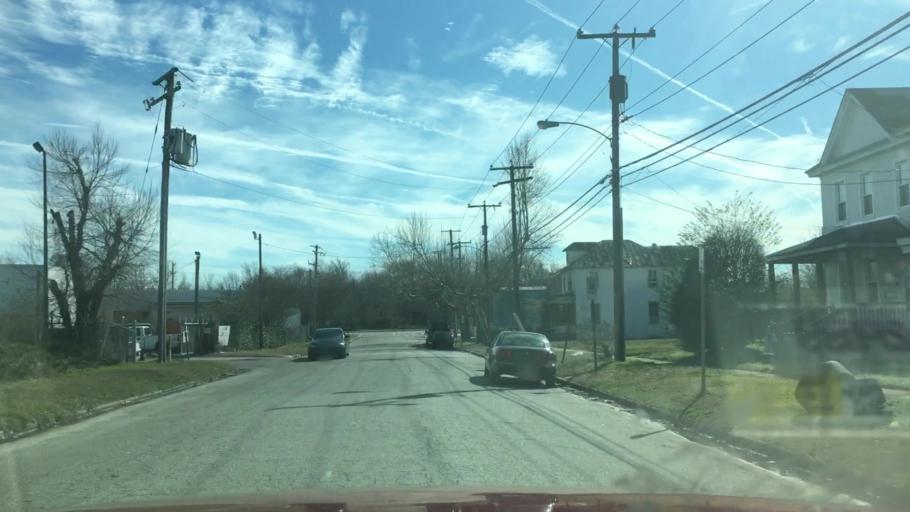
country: US
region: Virginia
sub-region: City of Portsmouth
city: Portsmouth
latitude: 36.8328
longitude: -76.3291
